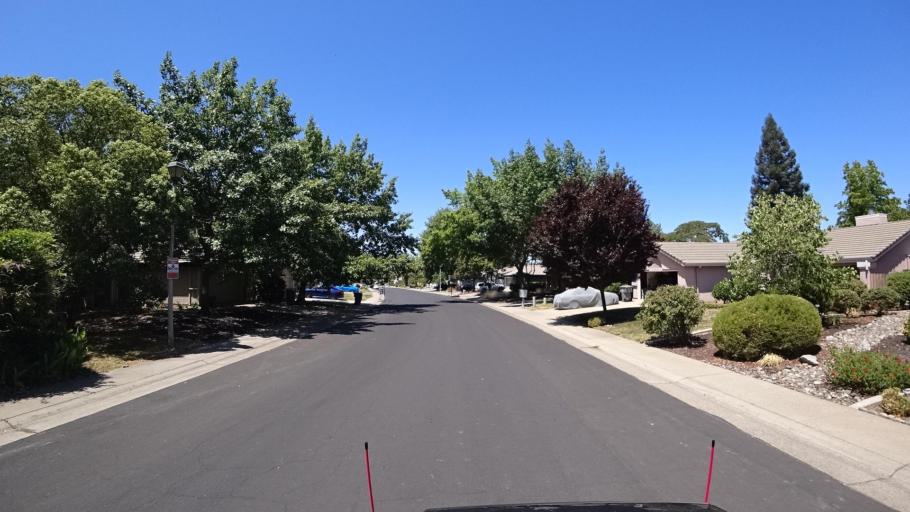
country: US
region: California
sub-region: Placer County
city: Rocklin
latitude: 38.8255
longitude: -121.2514
